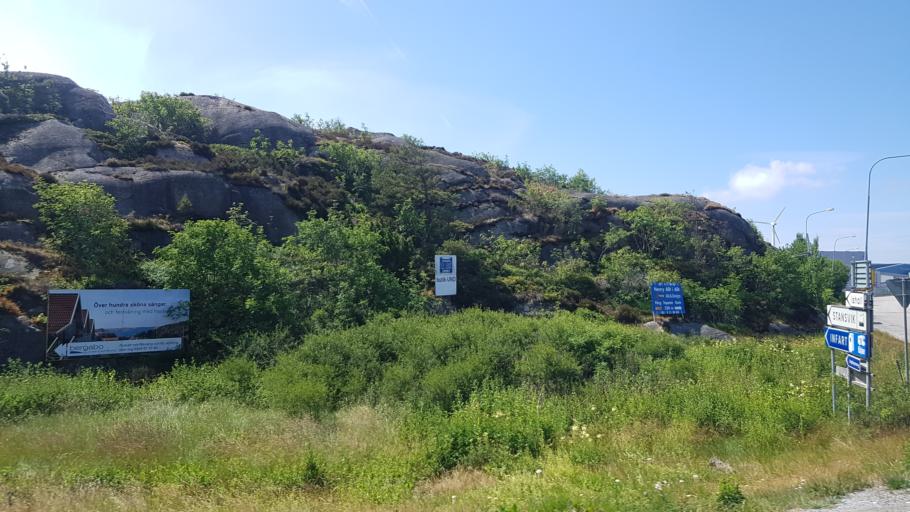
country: SE
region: Vaestra Goetaland
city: Ronnang
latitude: 57.9433
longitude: 11.5768
